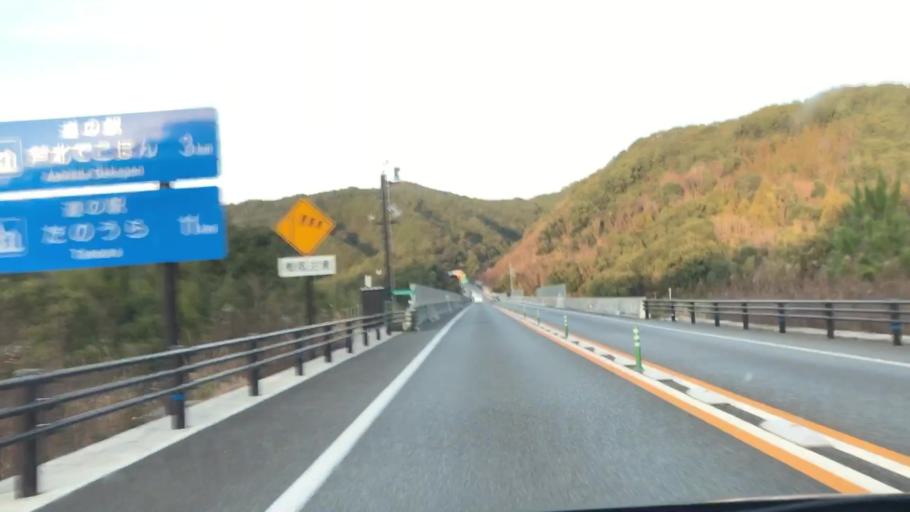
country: JP
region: Kumamoto
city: Minamata
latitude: 32.2782
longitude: 130.4972
